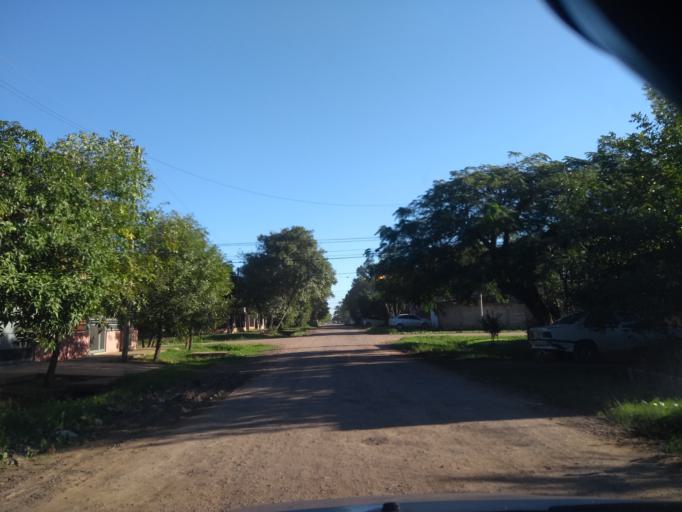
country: AR
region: Chaco
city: Barranqueras
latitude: -27.4845
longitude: -58.9466
